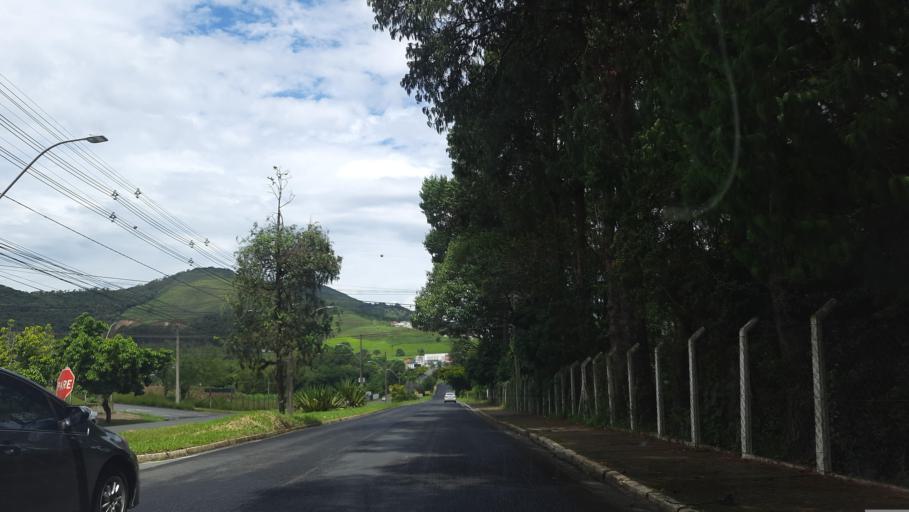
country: BR
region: Minas Gerais
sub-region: Pocos De Caldas
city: Pocos de Caldas
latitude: -21.7753
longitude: -46.6105
